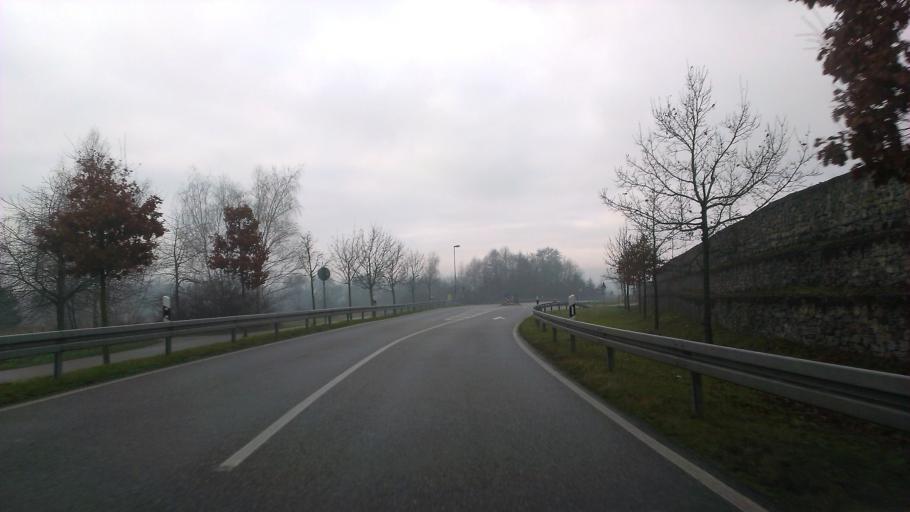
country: DE
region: Baden-Wuerttemberg
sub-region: Karlsruhe Region
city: Hambrucken
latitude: 49.2335
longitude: 8.5572
